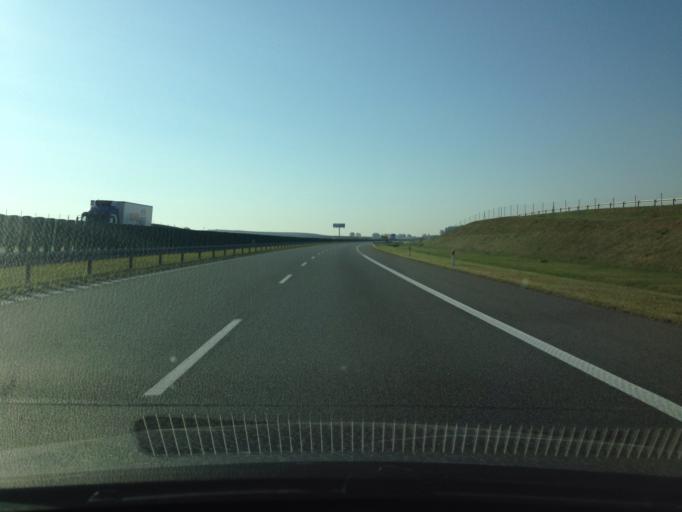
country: PL
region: Pomeranian Voivodeship
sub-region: Powiat tczewski
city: Pelplin
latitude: 53.9124
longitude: 18.6453
